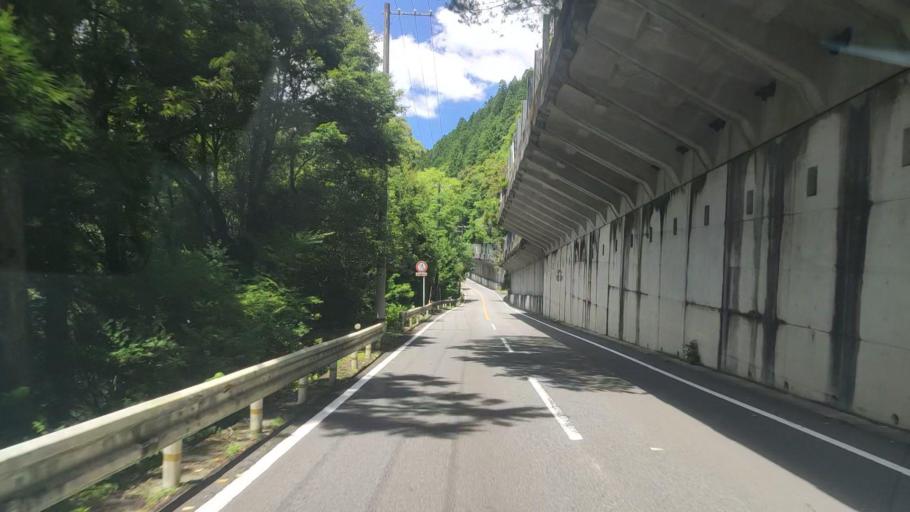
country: JP
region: Mie
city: Owase
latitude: 33.9984
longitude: 136.0115
